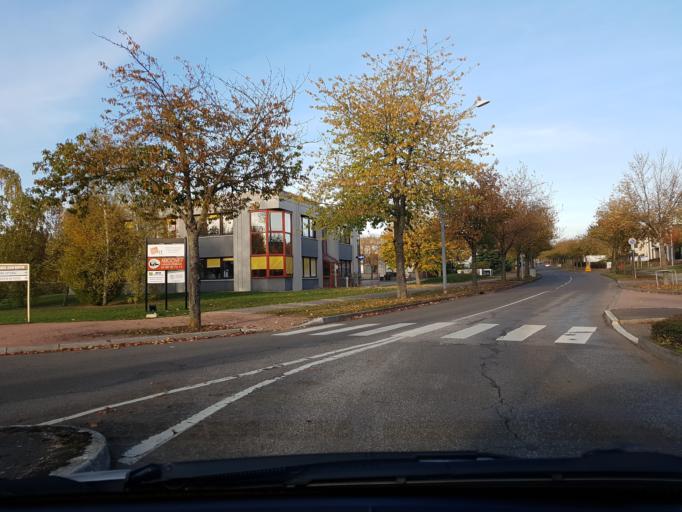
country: FR
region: Bourgogne
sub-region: Departement de la Cote-d'Or
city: Fontaine-les-Dijon
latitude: 47.3546
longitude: 5.0409
